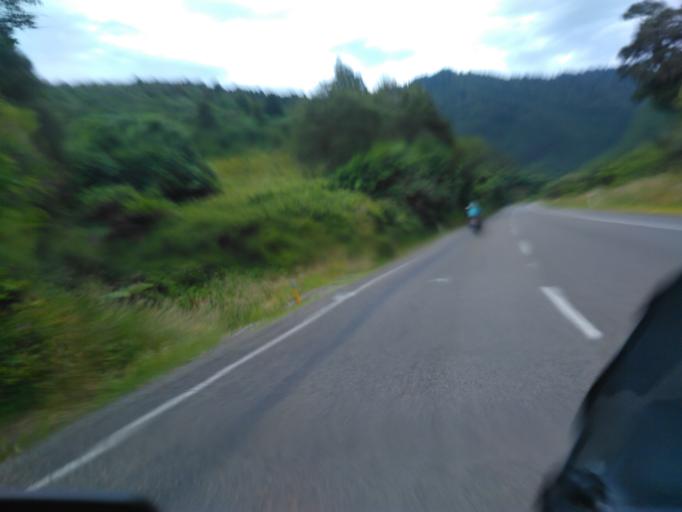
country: NZ
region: Bay of Plenty
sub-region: Opotiki District
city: Opotiki
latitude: -38.2887
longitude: 177.3761
